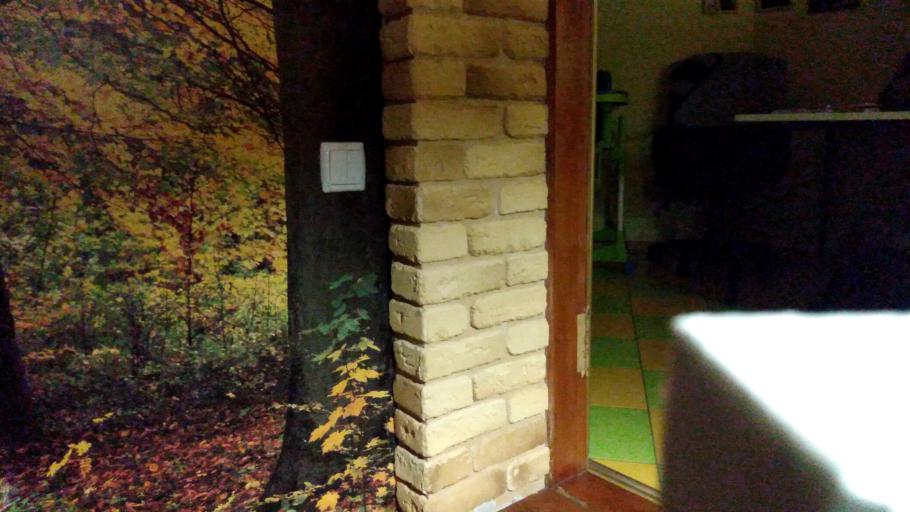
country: RU
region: Vologda
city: Lipin Bor
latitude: 61.1497
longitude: 37.9067
